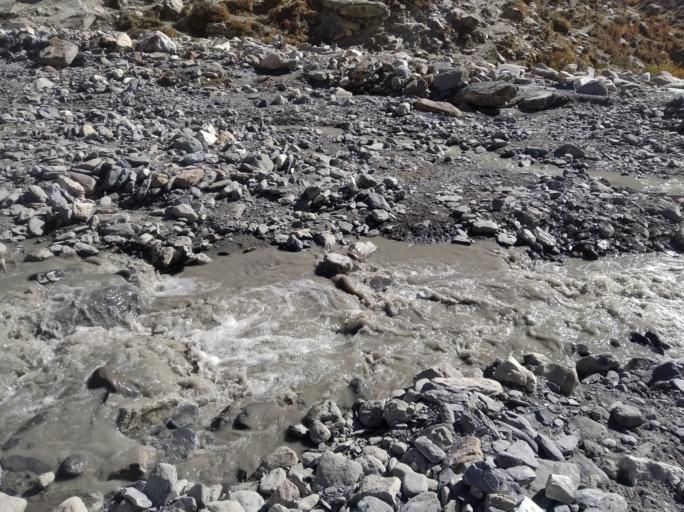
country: NP
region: Western Region
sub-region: Dhawalagiri Zone
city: Jomsom
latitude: 28.8319
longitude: 83.3932
